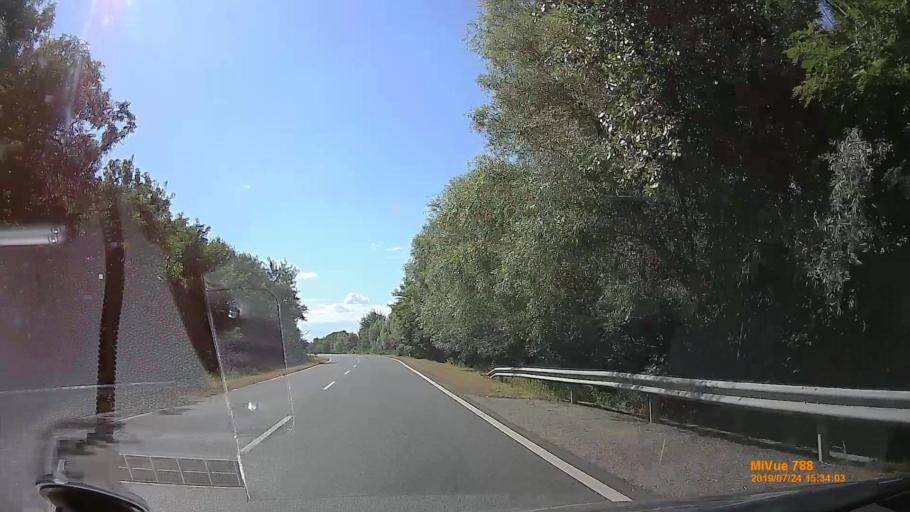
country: HU
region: Szabolcs-Szatmar-Bereg
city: Vasarosnameny
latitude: 48.1520
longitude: 22.3805
